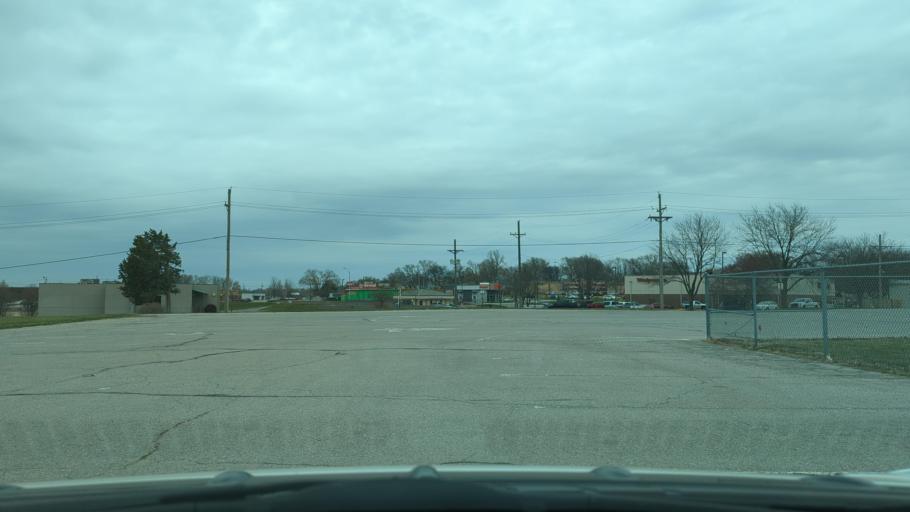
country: US
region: Nebraska
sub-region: Sarpy County
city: Bellevue
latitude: 41.1394
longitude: -95.9108
